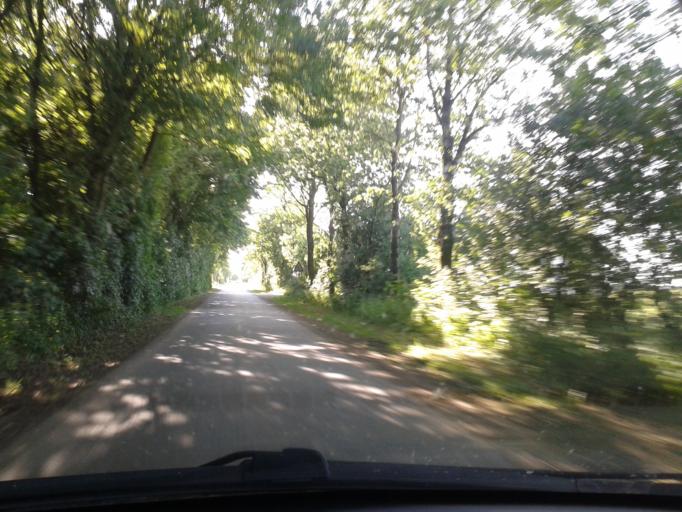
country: DE
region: North Rhine-Westphalia
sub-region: Regierungsbezirk Detmold
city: Schlangen
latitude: 51.7824
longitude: 8.8524
